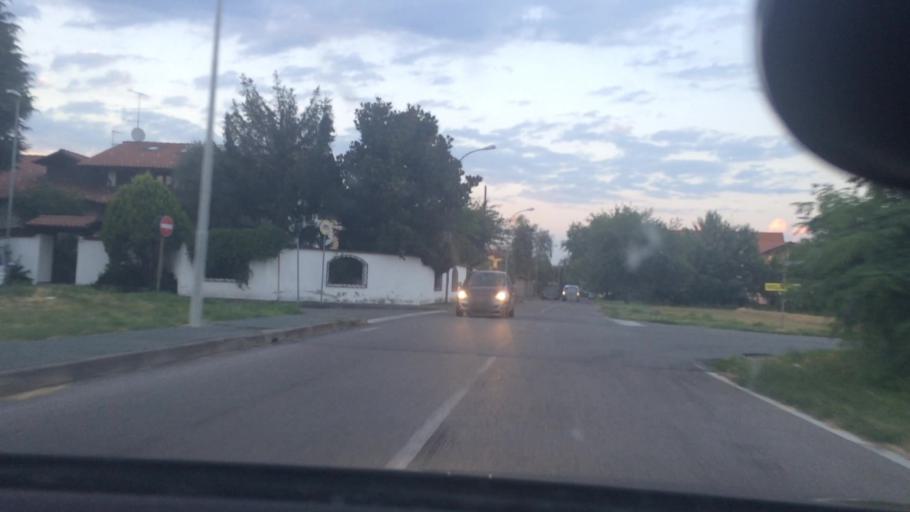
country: IT
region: Lombardy
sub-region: Citta metropolitana di Milano
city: Parabiago
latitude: 45.5455
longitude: 8.9458
